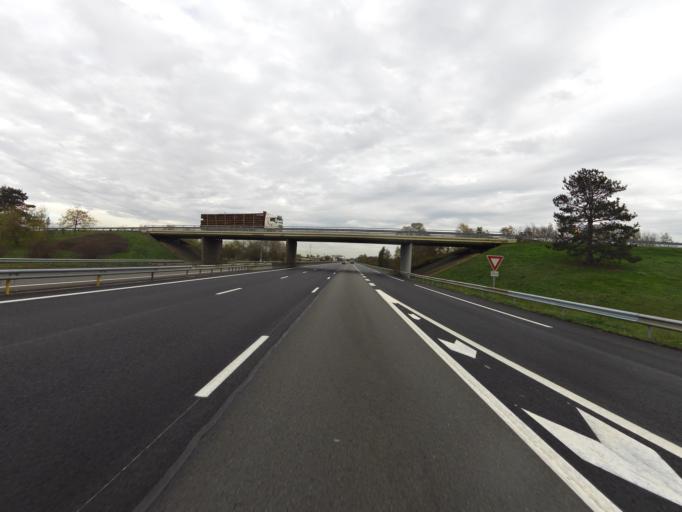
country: FR
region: Rhone-Alpes
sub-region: Departement du Rhone
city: Belleville
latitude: 46.1002
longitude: 4.7505
